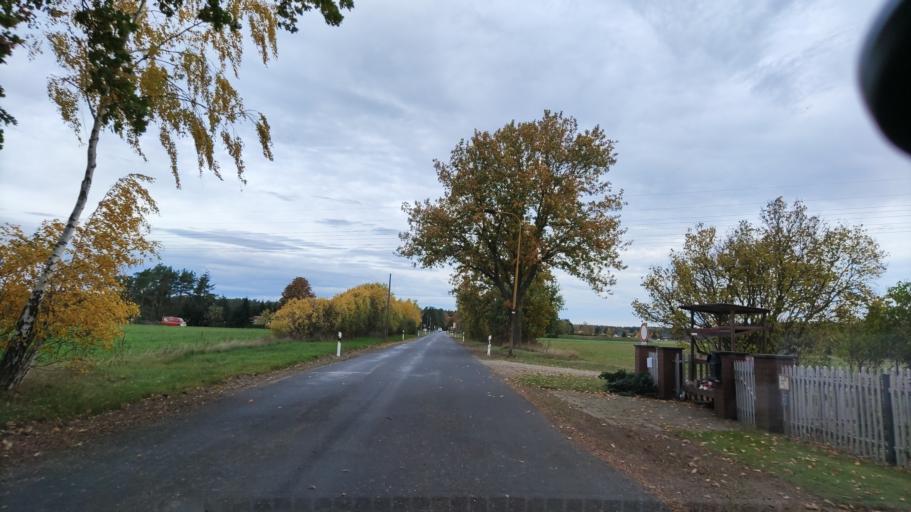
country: DE
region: Lower Saxony
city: Neu Darchau
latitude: 53.3670
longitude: 10.8634
